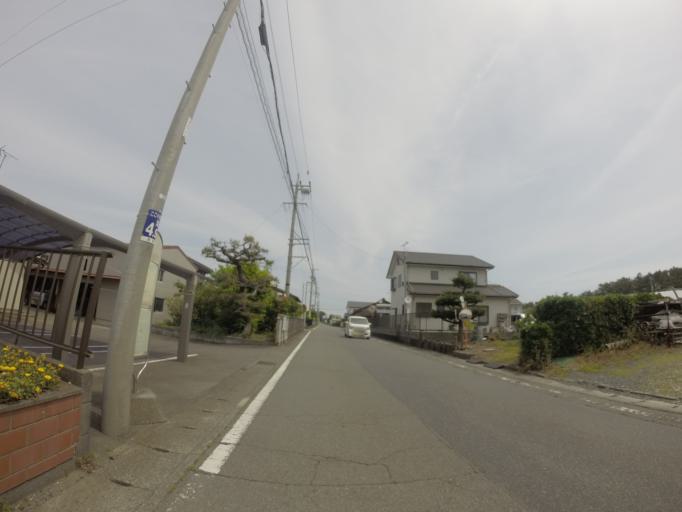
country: JP
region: Shizuoka
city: Yaizu
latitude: 34.7993
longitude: 138.3118
